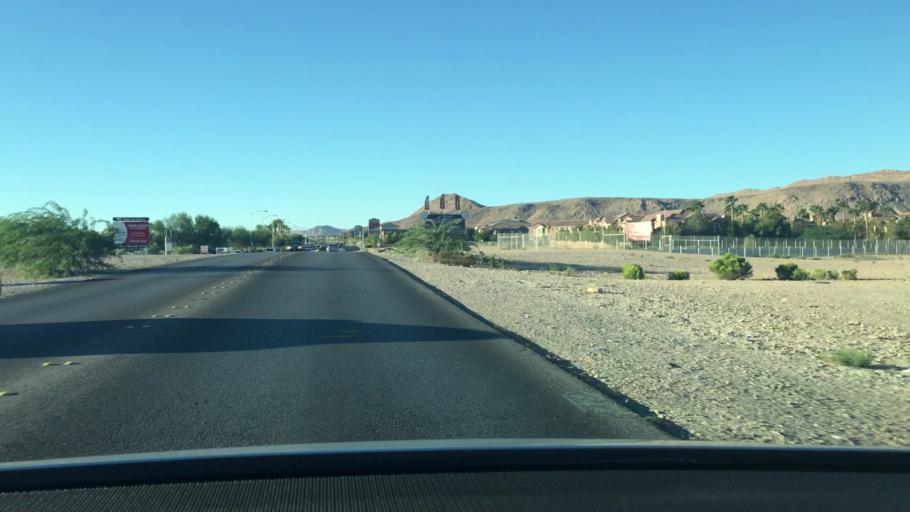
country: US
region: Nevada
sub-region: Clark County
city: Summerlin South
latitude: 36.0755
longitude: -115.2977
